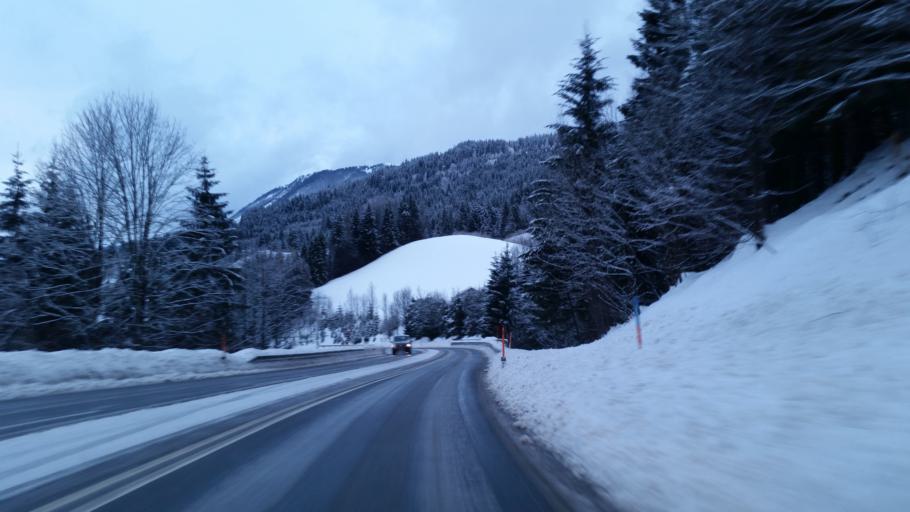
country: AT
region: Tyrol
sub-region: Politischer Bezirk Kitzbuhel
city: Fieberbrunn
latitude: 47.4698
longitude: 12.5647
